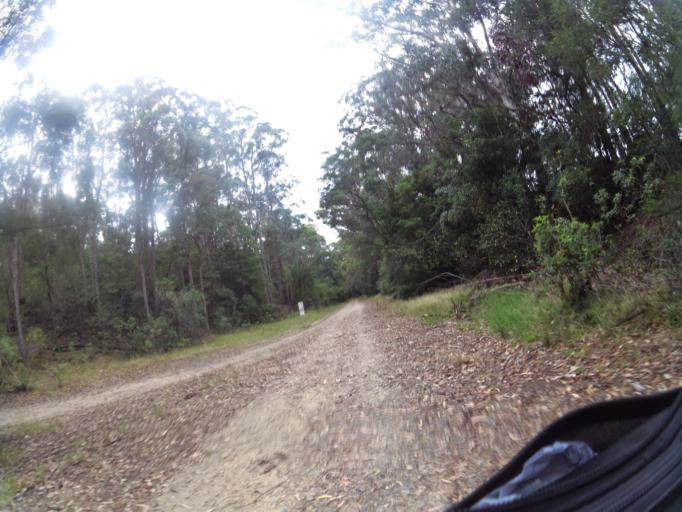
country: AU
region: Victoria
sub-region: East Gippsland
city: Lakes Entrance
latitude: -37.7355
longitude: 148.4244
